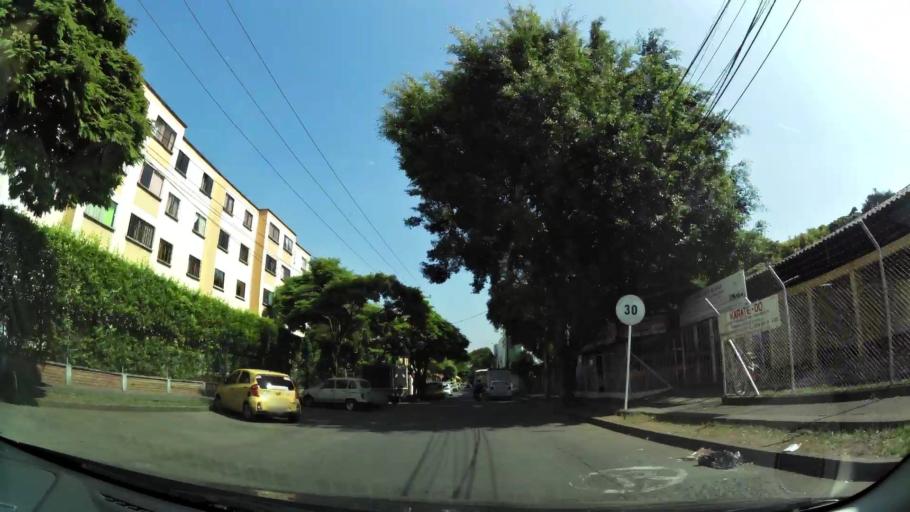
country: CO
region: Valle del Cauca
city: Cali
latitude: 3.4002
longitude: -76.5249
